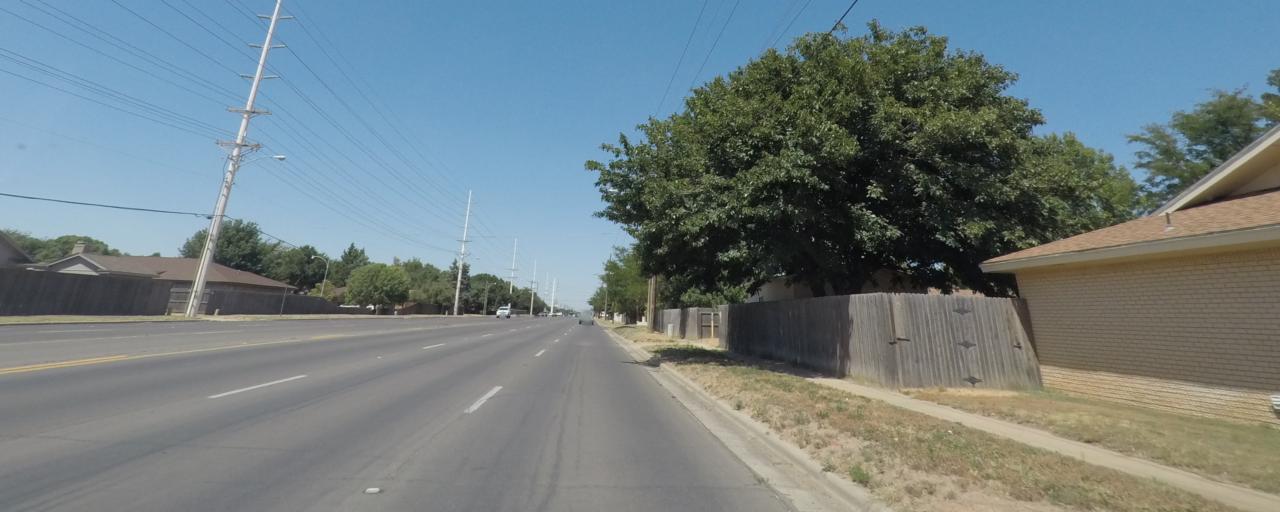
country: US
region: Texas
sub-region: Lubbock County
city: Lubbock
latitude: 33.5144
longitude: -101.8876
